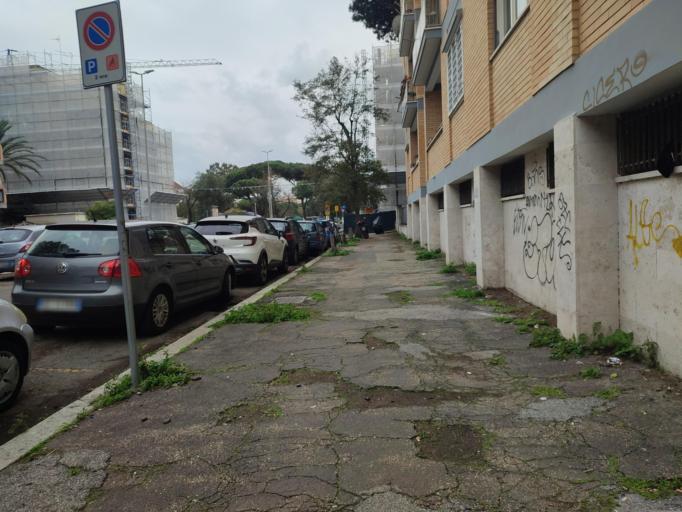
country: IT
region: Latium
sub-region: Citta metropolitana di Roma Capitale
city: Lido di Ostia
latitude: 41.7367
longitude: 12.2884
